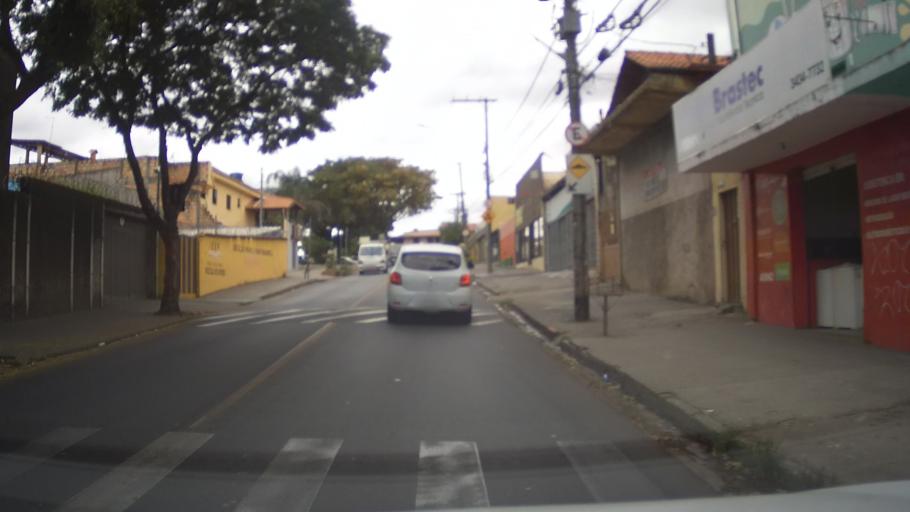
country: BR
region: Minas Gerais
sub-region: Belo Horizonte
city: Belo Horizonte
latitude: -19.8339
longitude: -43.9373
